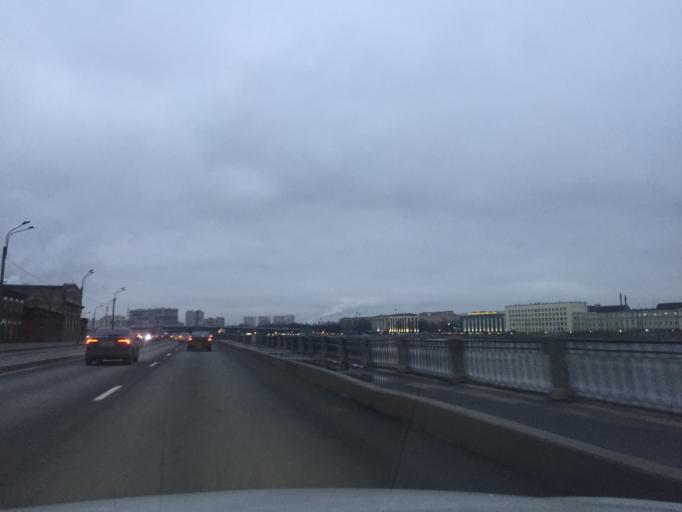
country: RU
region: St.-Petersburg
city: Obukhovo
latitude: 59.8851
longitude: 30.4493
